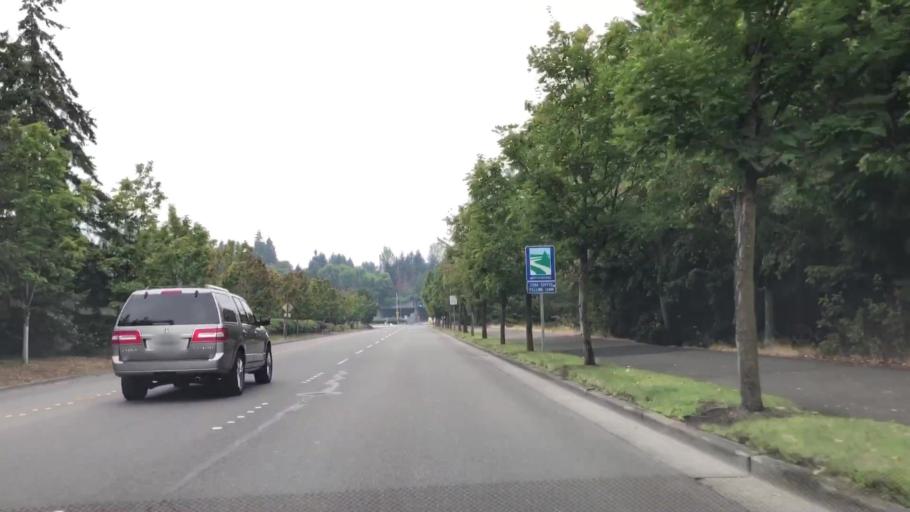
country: US
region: Washington
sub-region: King County
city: Mercer Island
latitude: 47.5893
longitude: -122.2347
